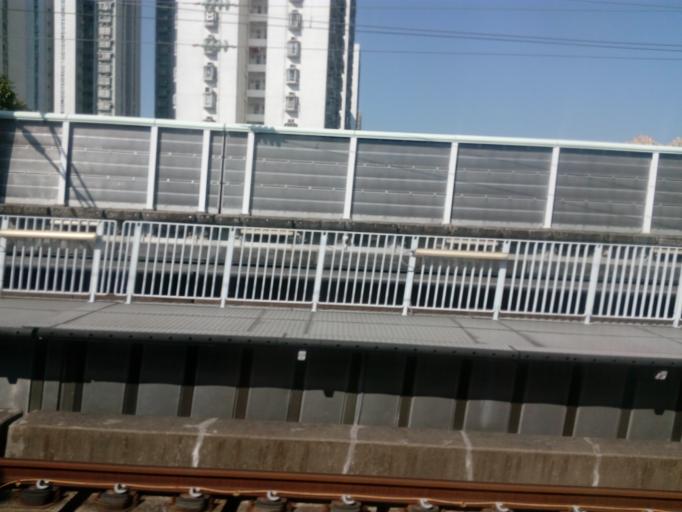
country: HK
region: Sha Tin
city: Sha Tin
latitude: 22.3858
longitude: 114.2064
